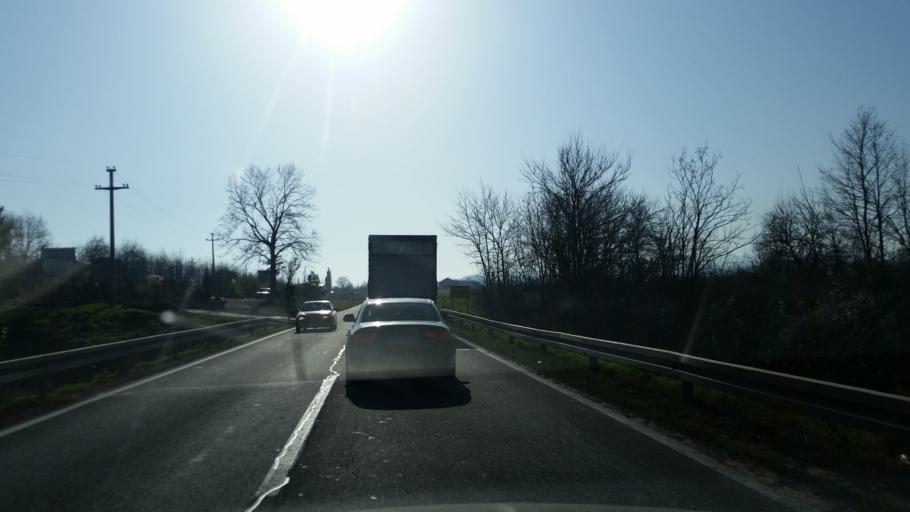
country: RS
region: Central Serbia
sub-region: Kolubarski Okrug
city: Ljig
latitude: 44.2670
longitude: 20.2849
